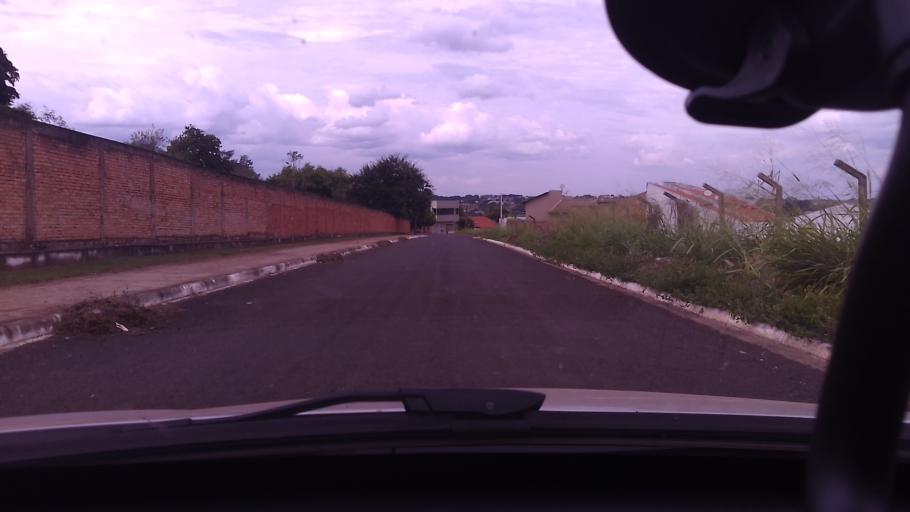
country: BR
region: Goias
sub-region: Mineiros
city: Mineiros
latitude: -17.5679
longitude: -52.5700
